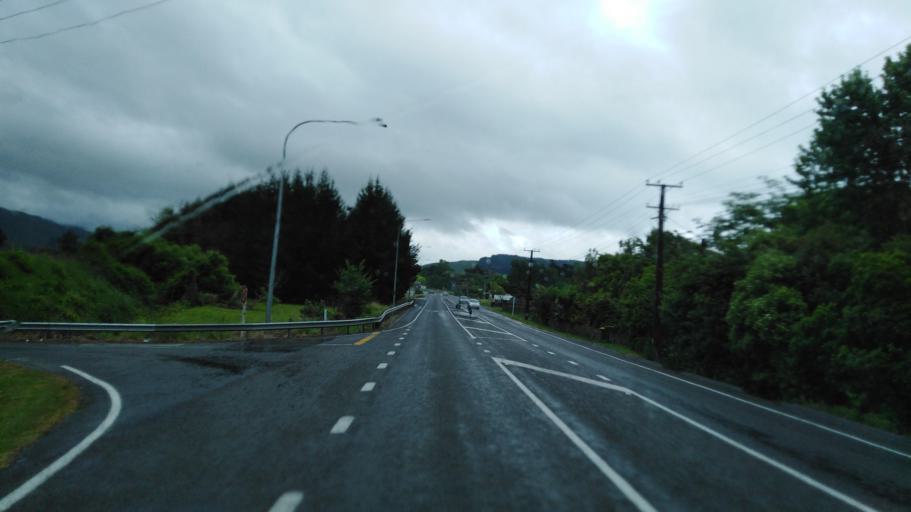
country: NZ
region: Wellington
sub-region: Kapiti Coast District
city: Otaki
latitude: -40.7175
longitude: 175.2147
